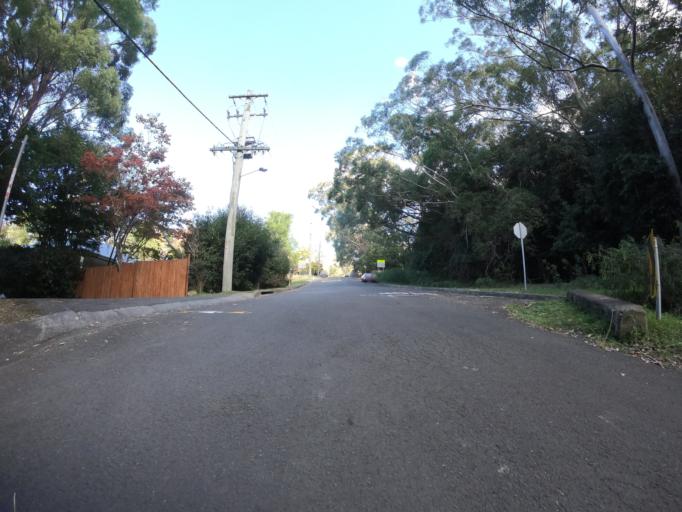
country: AU
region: New South Wales
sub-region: Wollongong
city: Cordeaux Heights
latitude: -34.4297
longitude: 150.8179
